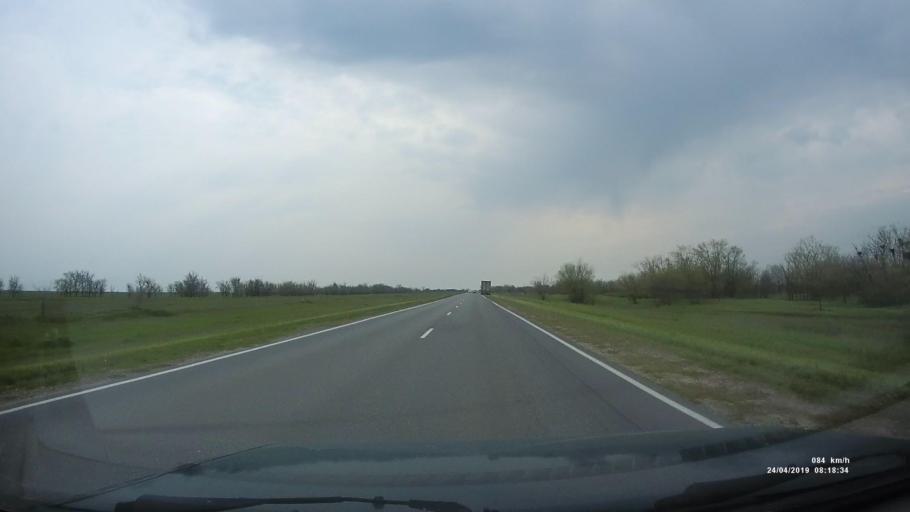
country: RU
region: Kalmykiya
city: Priyutnoye
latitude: 46.1012
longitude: 43.6500
